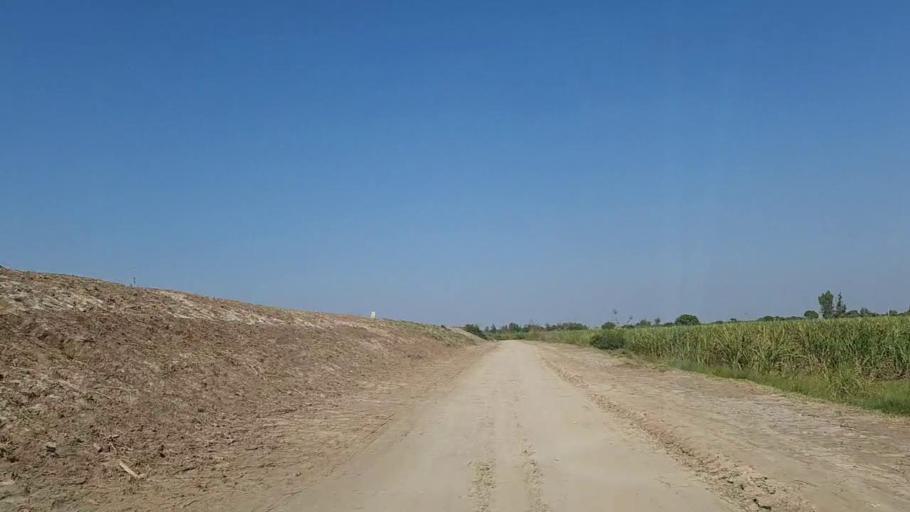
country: PK
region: Sindh
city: Chuhar Jamali
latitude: 24.5799
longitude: 68.0302
